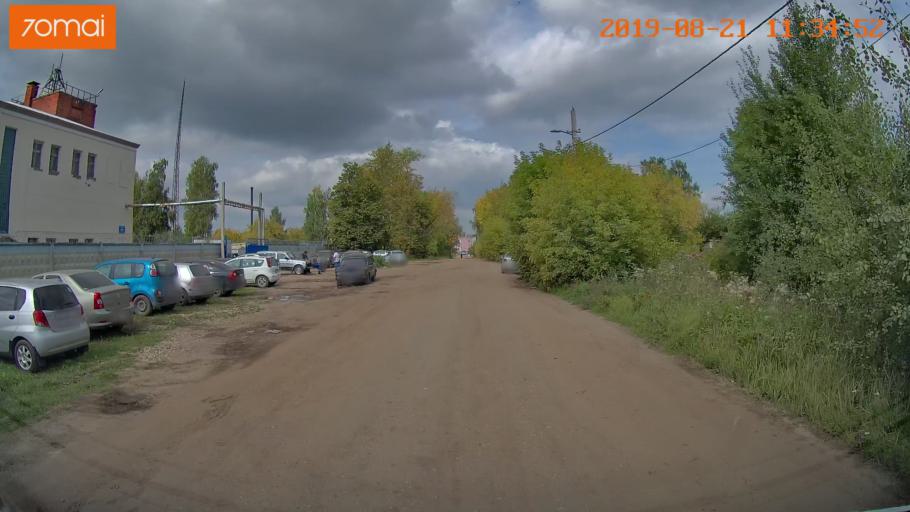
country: RU
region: Ivanovo
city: Novo-Talitsy
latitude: 56.9888
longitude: 40.9116
